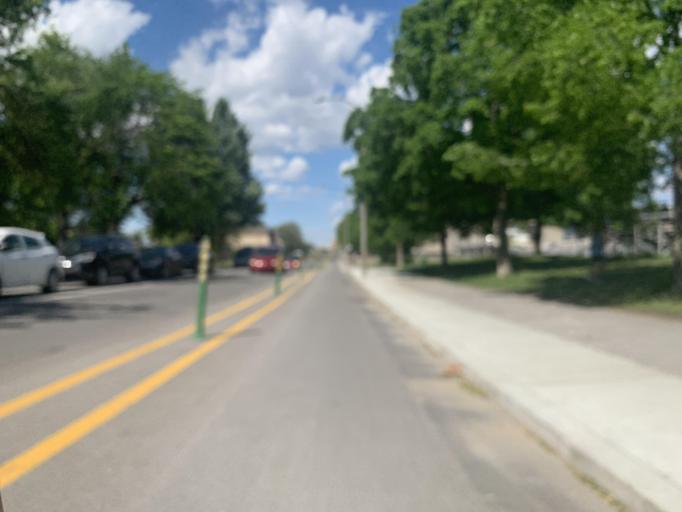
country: CA
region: Quebec
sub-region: Montreal
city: Montreal
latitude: 45.5395
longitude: -73.5953
